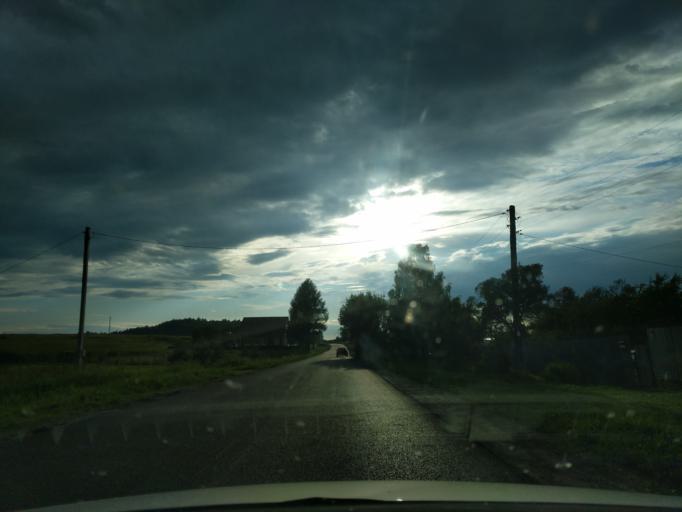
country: RU
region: Kaluga
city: Myatlevo
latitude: 54.8010
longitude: 35.7228
